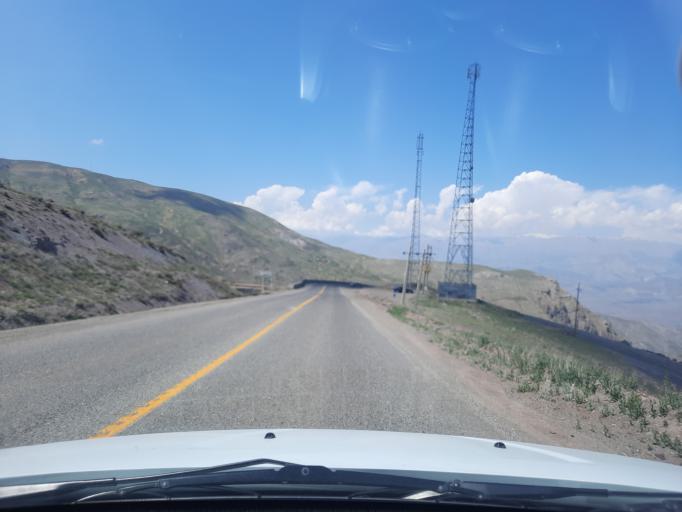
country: IR
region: Qazvin
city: Qazvin
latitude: 36.4059
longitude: 50.2216
